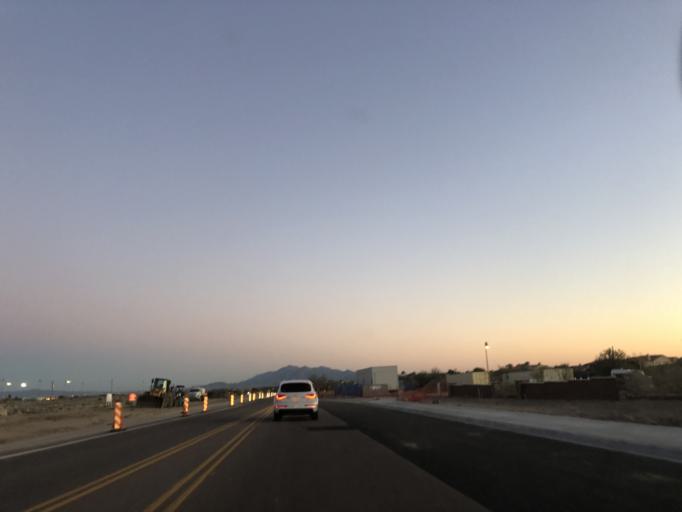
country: US
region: Arizona
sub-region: Maricopa County
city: Citrus Park
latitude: 33.4985
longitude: -112.5026
